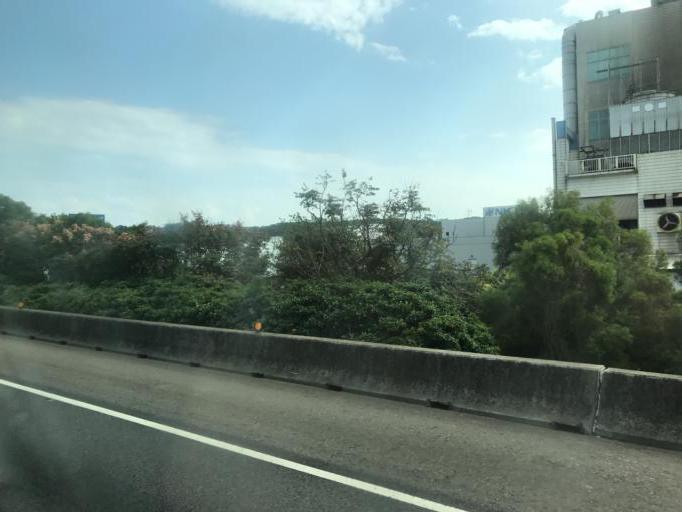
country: TW
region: Taiwan
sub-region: Hsinchu
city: Zhubei
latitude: 24.8770
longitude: 121.0384
